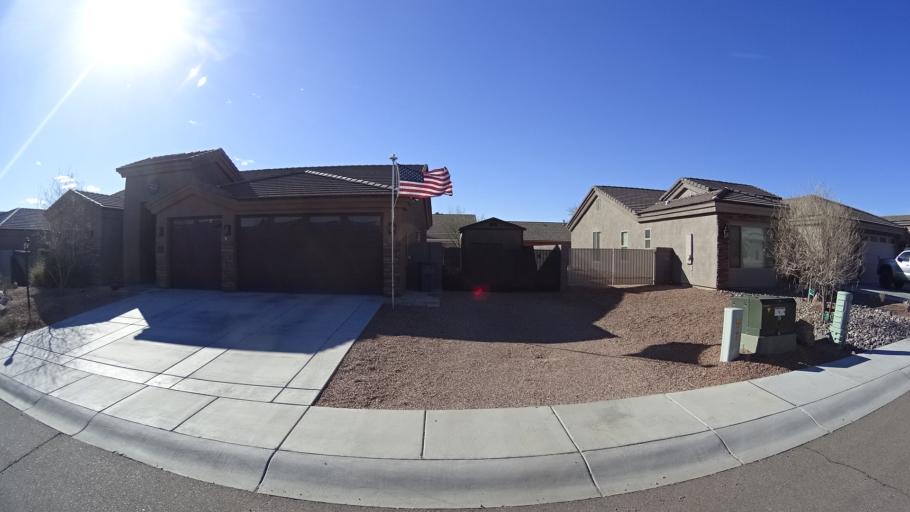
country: US
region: Arizona
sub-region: Mohave County
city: New Kingman-Butler
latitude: 35.2376
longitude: -114.0320
